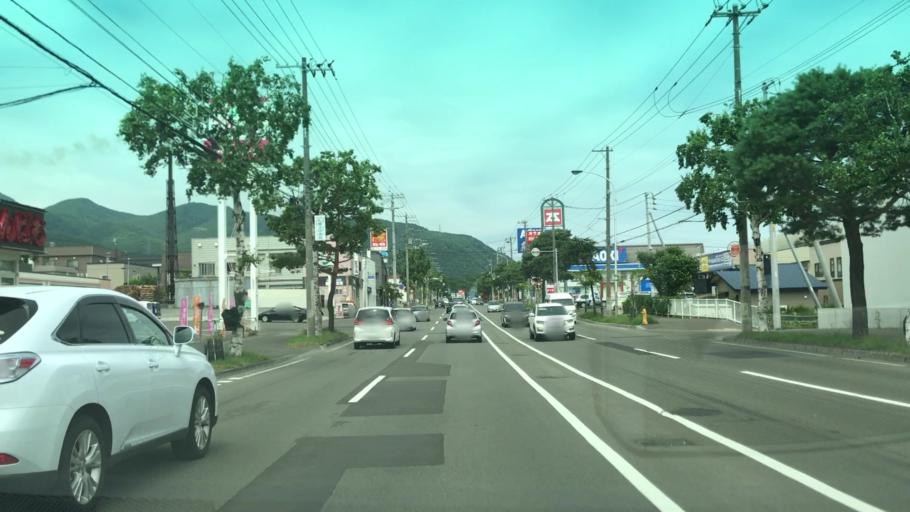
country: JP
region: Hokkaido
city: Sapporo
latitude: 43.0740
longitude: 141.2788
